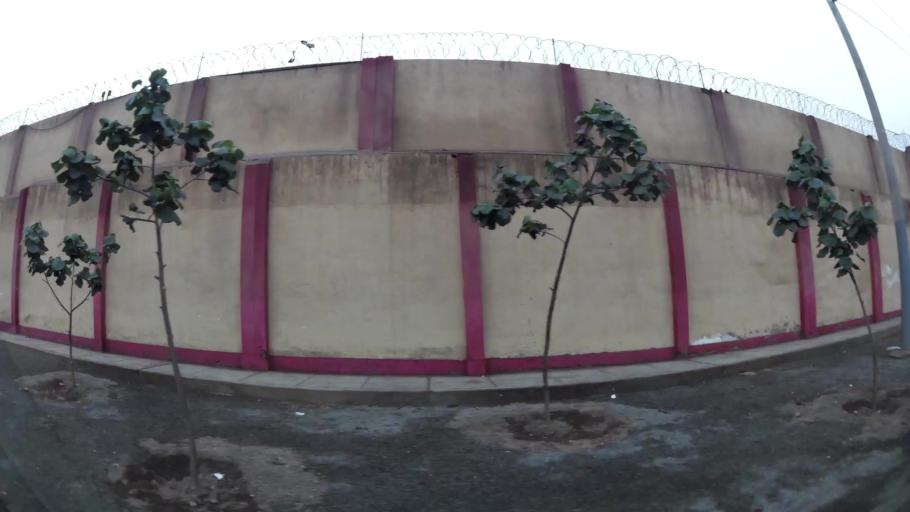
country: PE
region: Callao
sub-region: Callao
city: Callao
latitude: -12.0840
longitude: -77.1000
